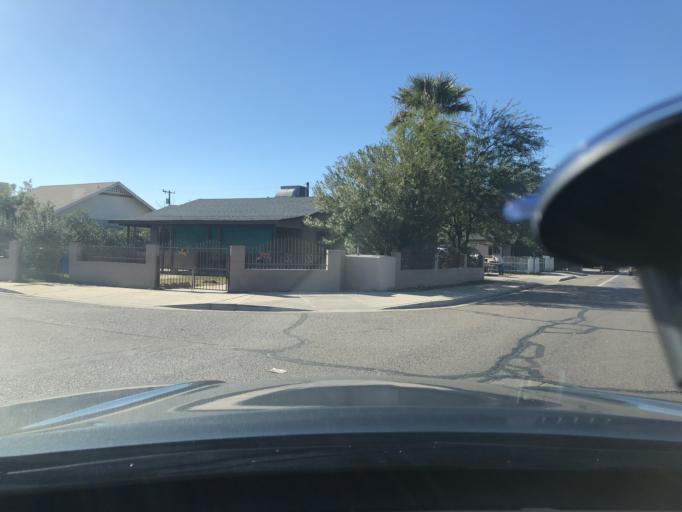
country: US
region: Arizona
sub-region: Maricopa County
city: Phoenix
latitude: 33.4731
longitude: -112.0277
